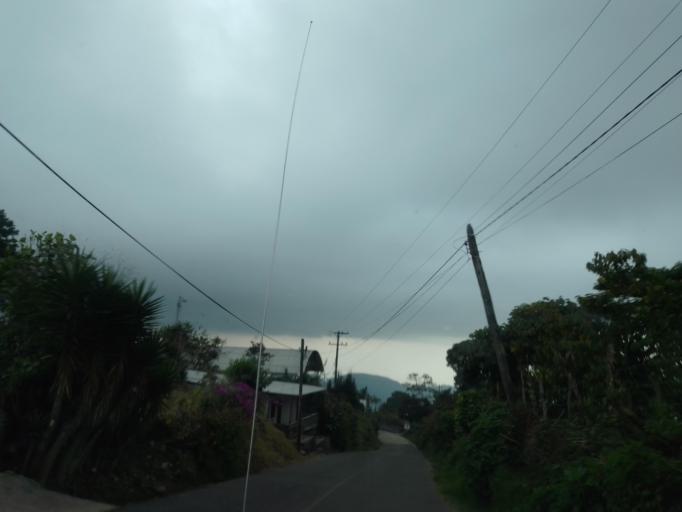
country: MX
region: Chiapas
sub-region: Union Juarez
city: Santo Domingo
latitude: 15.0683
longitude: -92.0816
